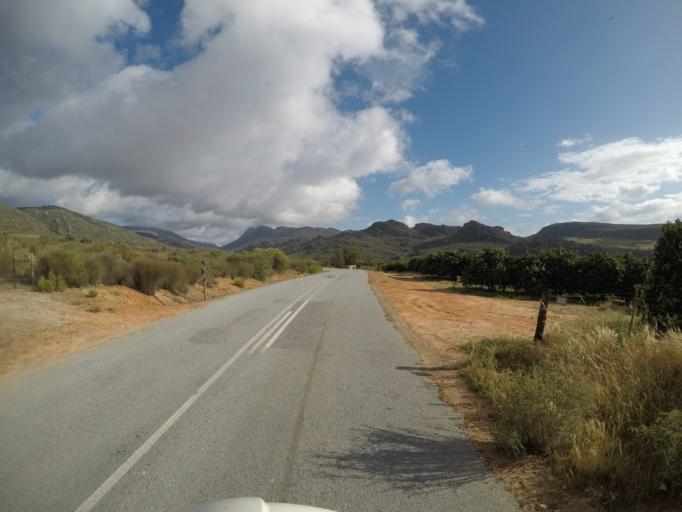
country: ZA
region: Western Cape
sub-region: West Coast District Municipality
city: Clanwilliam
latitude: -32.4269
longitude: 18.9368
